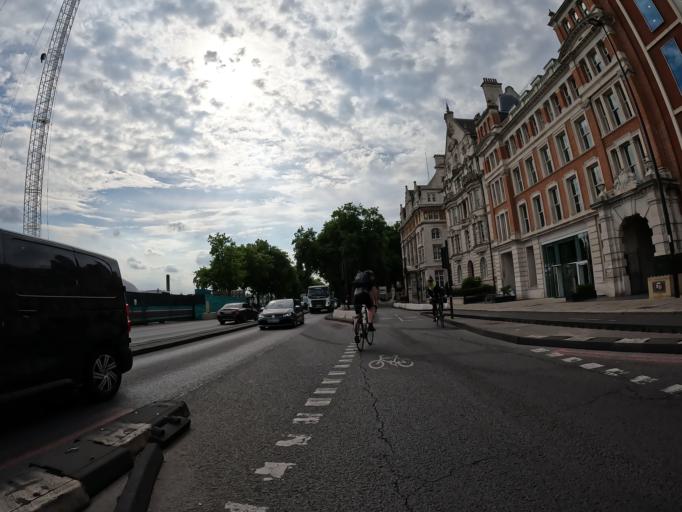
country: GB
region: England
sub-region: Greater London
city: Islington
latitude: 51.5337
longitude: -0.0966
